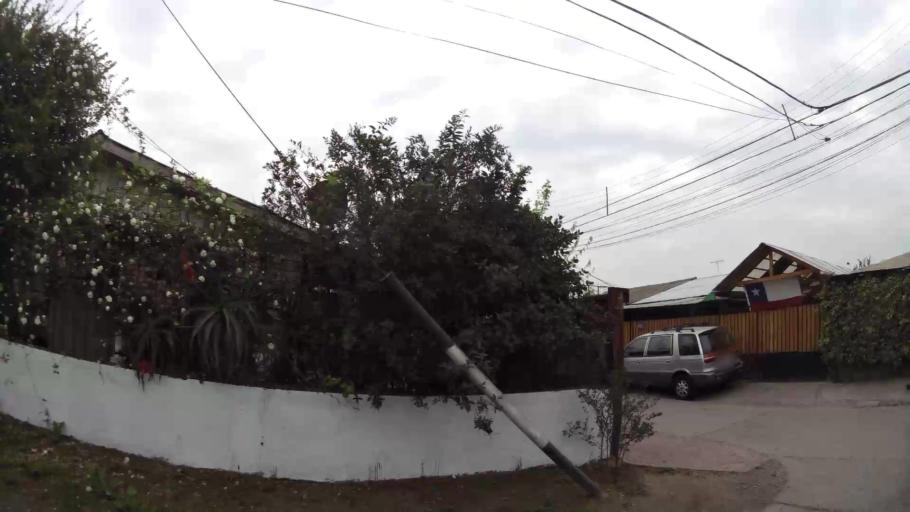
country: CL
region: Santiago Metropolitan
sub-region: Provincia de Santiago
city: Villa Presidente Frei, Nunoa, Santiago, Chile
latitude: -33.4966
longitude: -70.6010
